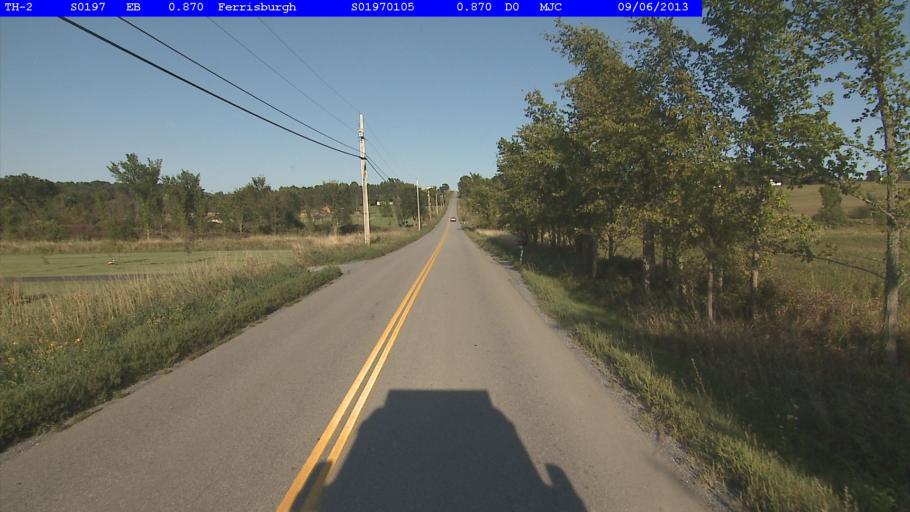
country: US
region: Vermont
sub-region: Addison County
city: Vergennes
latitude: 44.1739
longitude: -73.2220
